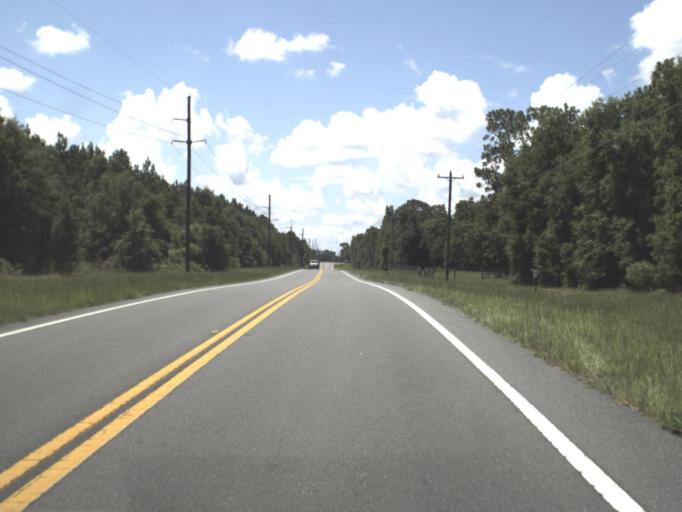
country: US
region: Florida
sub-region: Alachua County
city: Hawthorne
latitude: 29.6374
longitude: -82.0316
